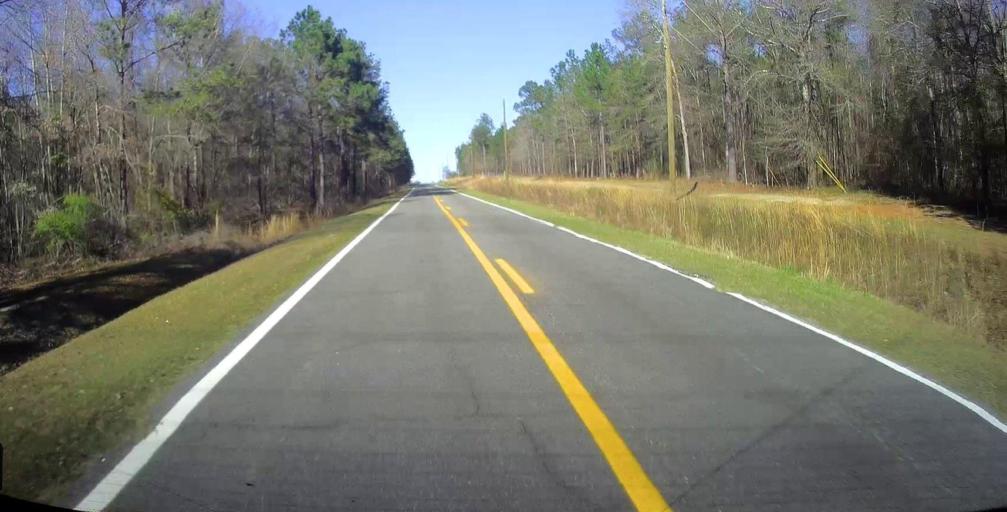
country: US
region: Georgia
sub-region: Taylor County
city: Reynolds
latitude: 32.5756
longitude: -83.9961
